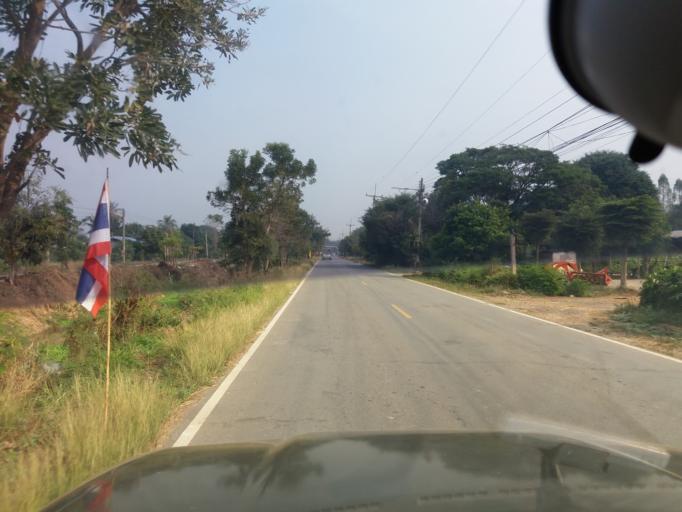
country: TH
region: Suphan Buri
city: Doem Bang Nang Buat
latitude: 14.9011
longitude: 100.1911
